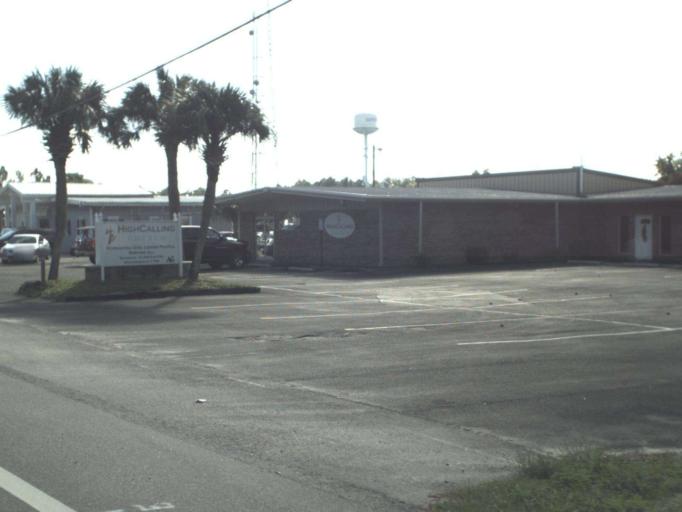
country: US
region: Florida
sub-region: Franklin County
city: Eastpoint
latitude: 29.7350
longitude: -84.8880
